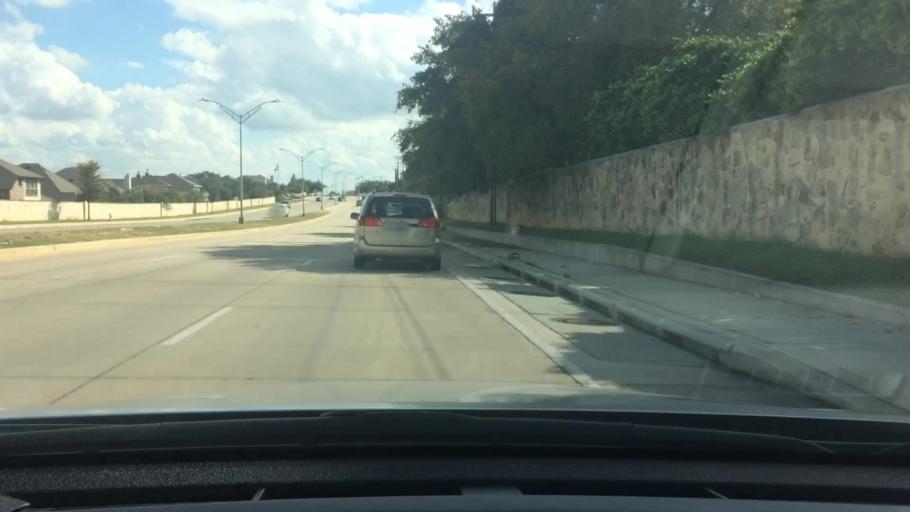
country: US
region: Texas
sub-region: Bexar County
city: Hollywood Park
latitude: 29.6143
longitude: -98.4219
